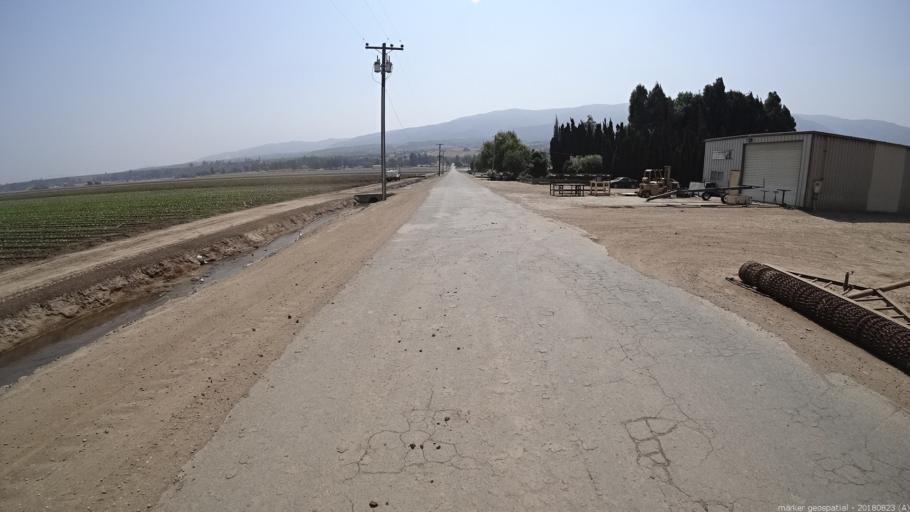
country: US
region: California
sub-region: Monterey County
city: Soledad
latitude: 36.4003
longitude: -121.3626
